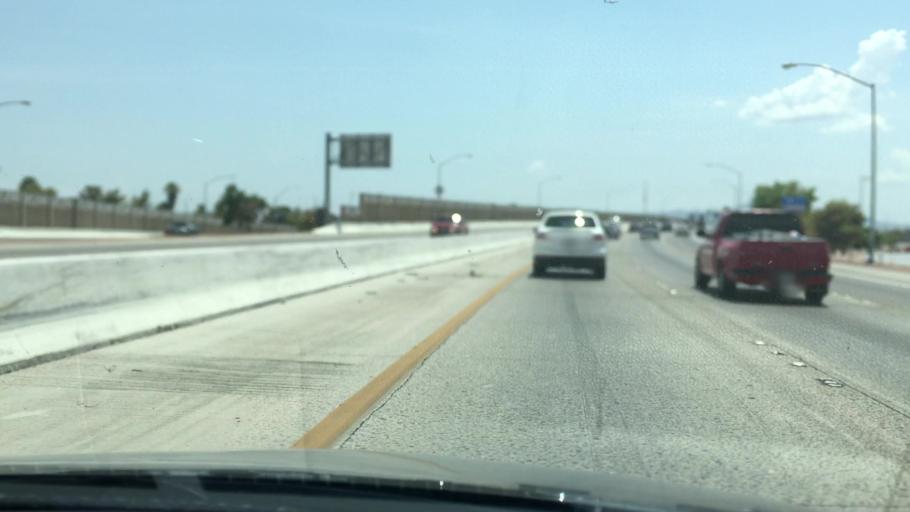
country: US
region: Nevada
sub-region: Clark County
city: Winchester
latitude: 36.1620
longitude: -115.0923
